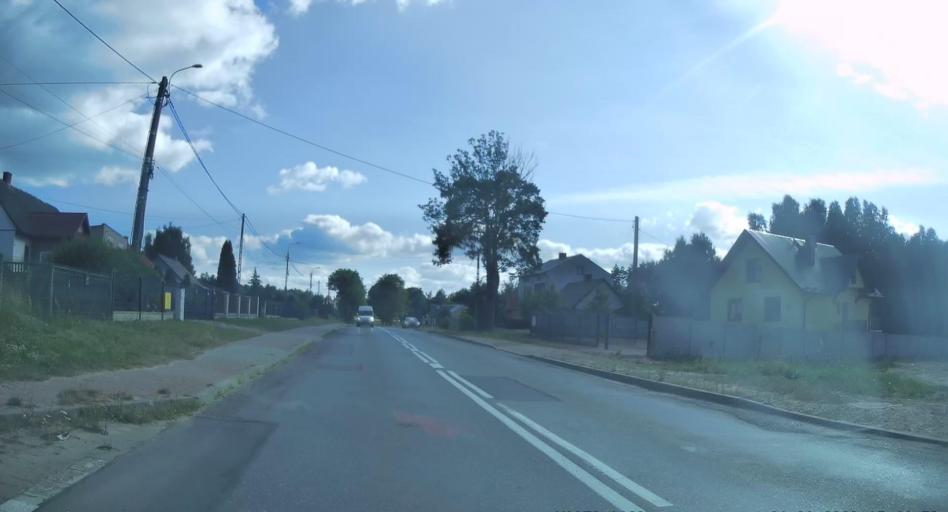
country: PL
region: Swietokrzyskie
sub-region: Powiat skarzyski
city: Suchedniow
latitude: 51.0305
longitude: 20.8393
